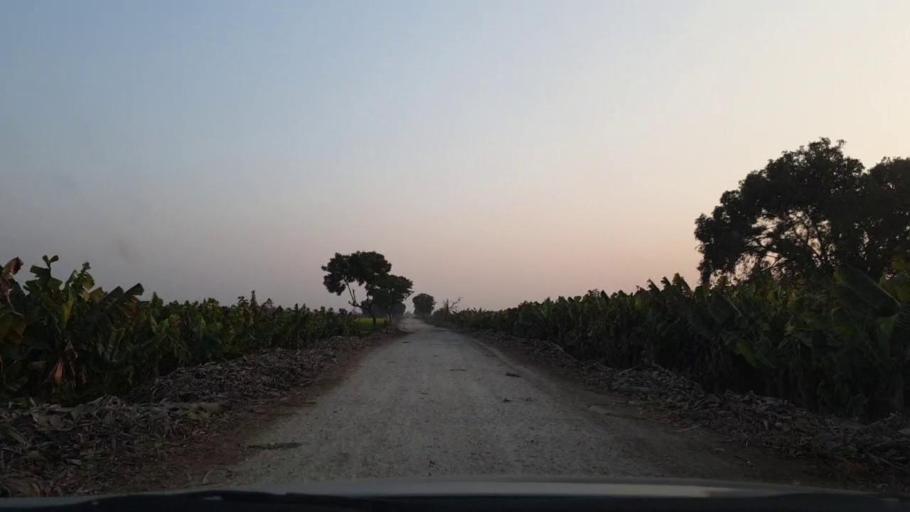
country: PK
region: Sindh
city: Matiari
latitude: 25.6843
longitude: 68.5241
